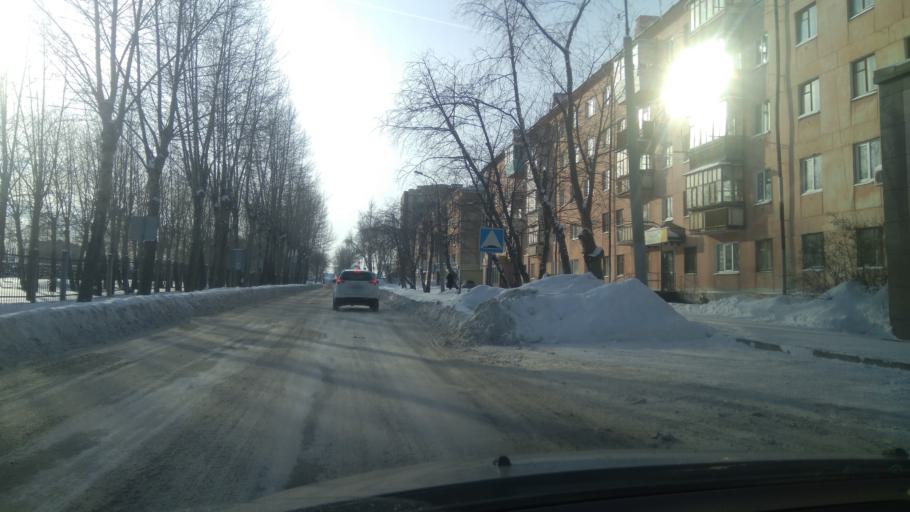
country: RU
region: Sverdlovsk
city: Sukhoy Log
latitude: 56.9016
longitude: 62.0299
